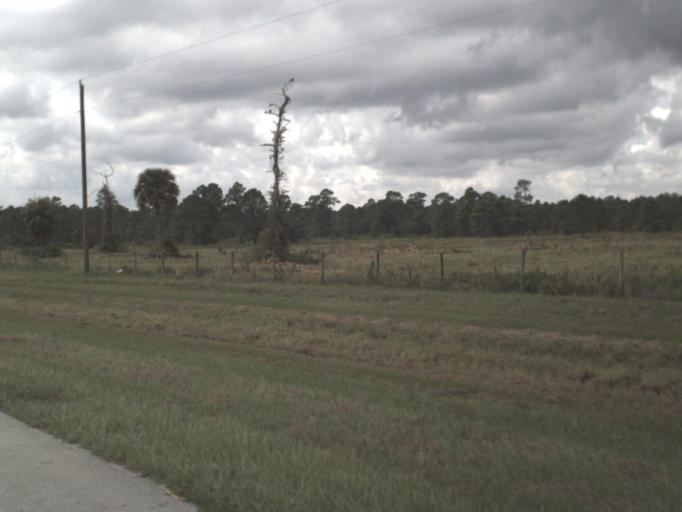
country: US
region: Florida
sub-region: Hendry County
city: Port LaBelle
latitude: 26.8976
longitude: -81.3392
